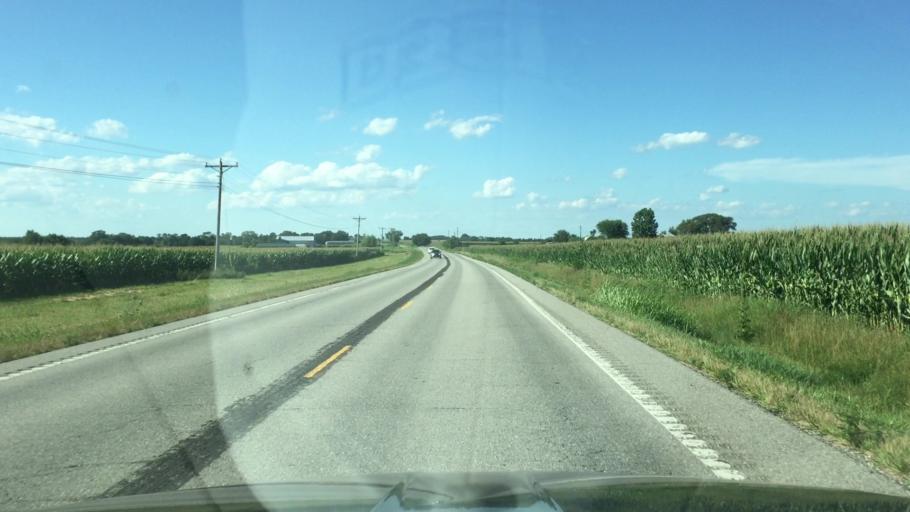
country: US
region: Missouri
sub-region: Moniteau County
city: Tipton
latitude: 38.5854
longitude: -92.7898
